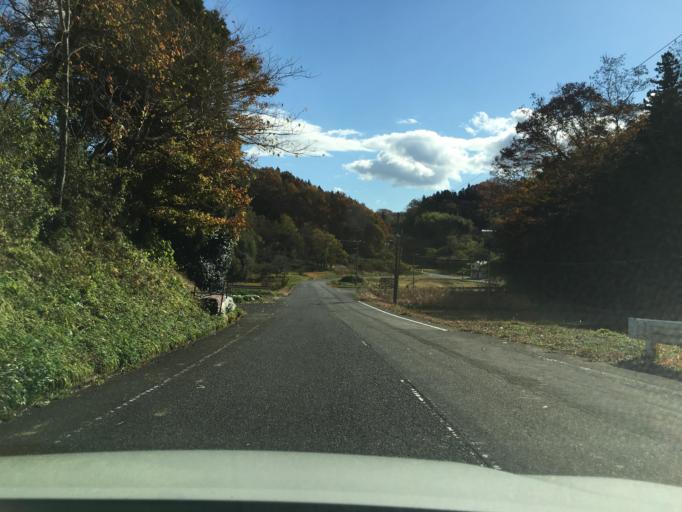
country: JP
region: Fukushima
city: Miharu
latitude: 37.4488
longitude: 140.4561
